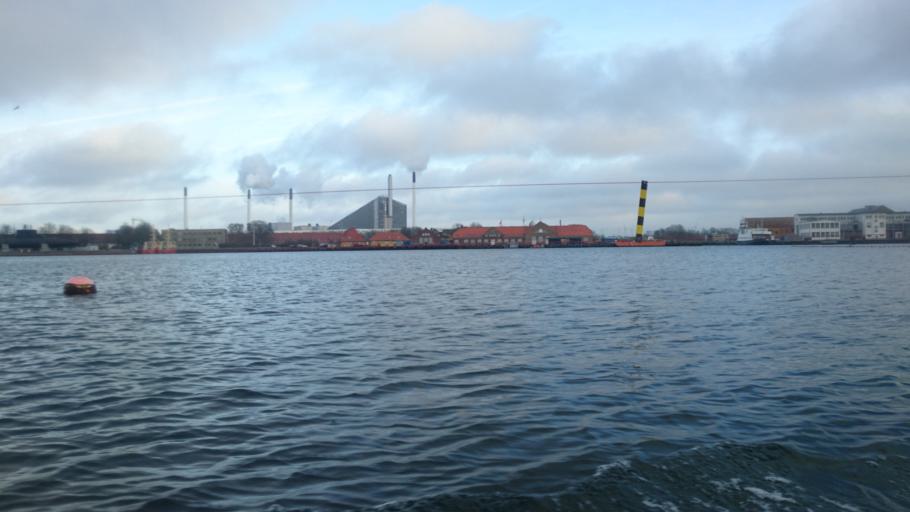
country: DK
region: Capital Region
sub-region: Kobenhavn
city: Christianshavn
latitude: 55.6858
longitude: 12.5994
